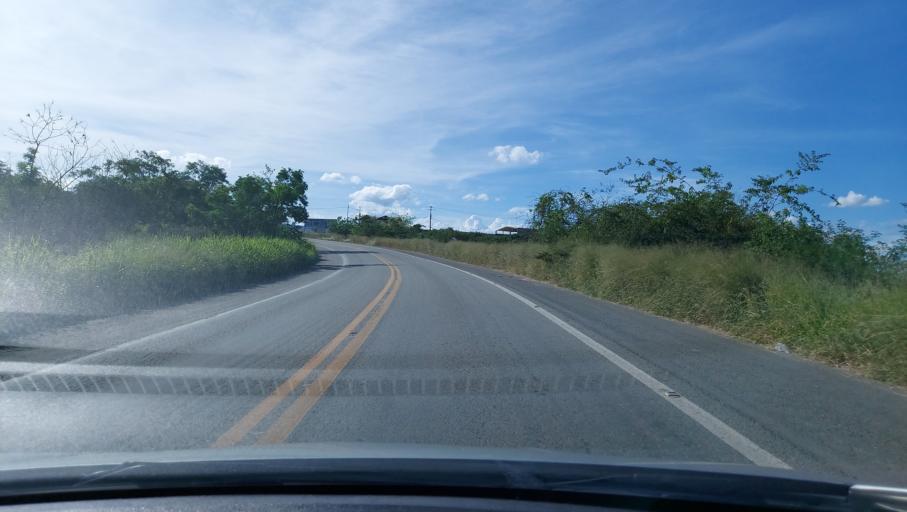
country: BR
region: Bahia
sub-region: Seabra
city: Seabra
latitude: -12.4272
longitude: -41.7624
